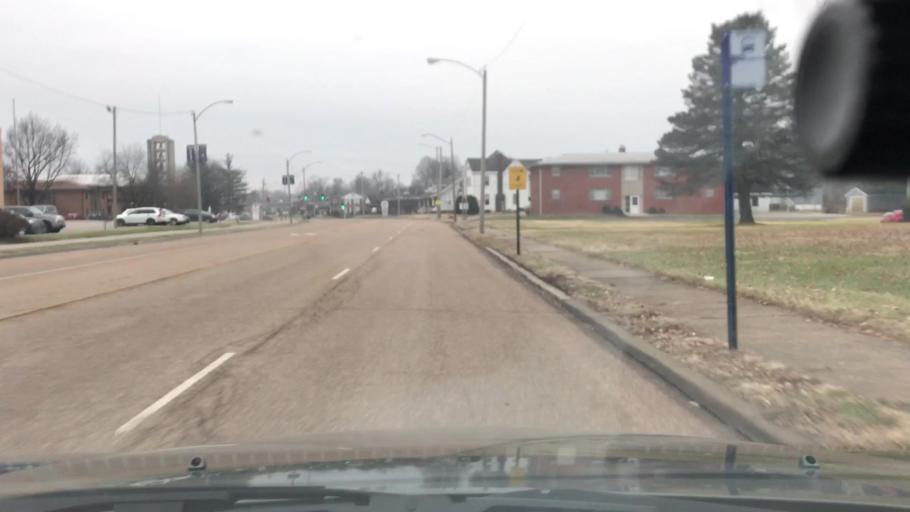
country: US
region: Illinois
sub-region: Saint Clair County
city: Swansea
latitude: 38.5477
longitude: -90.0336
